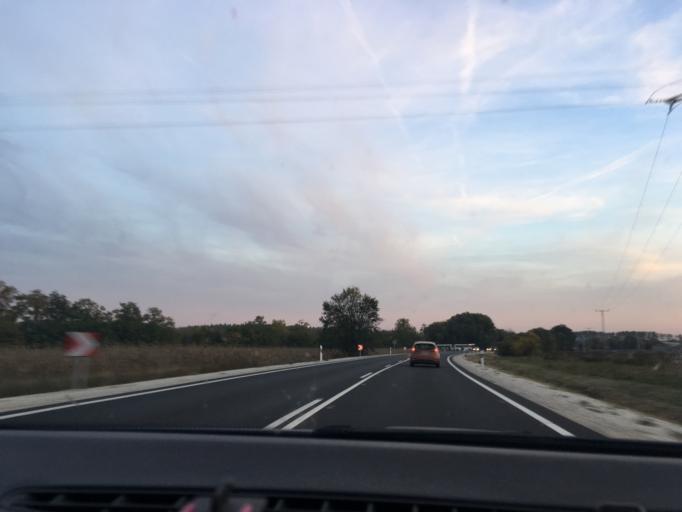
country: HU
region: Hajdu-Bihar
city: Hajduhadhaz
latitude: 47.6603
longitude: 21.6600
